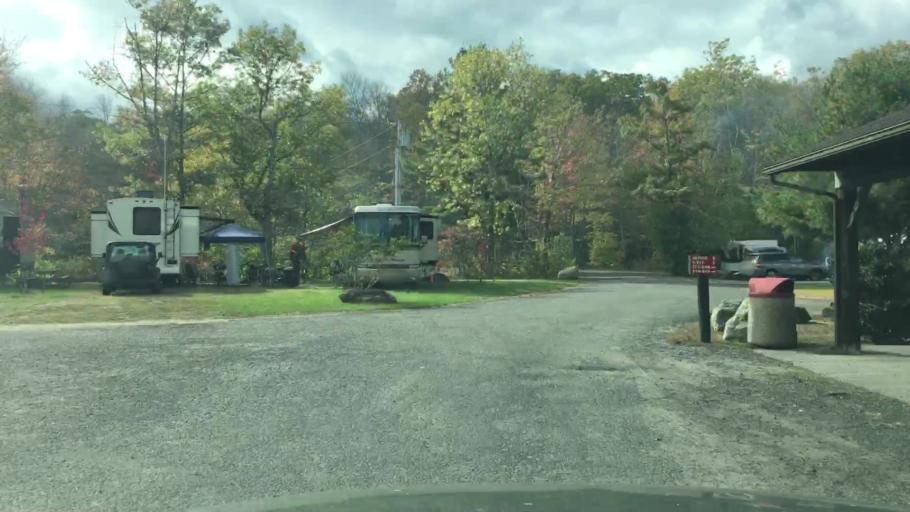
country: US
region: Connecticut
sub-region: Tolland County
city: Storrs
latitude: 41.8900
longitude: -72.1771
